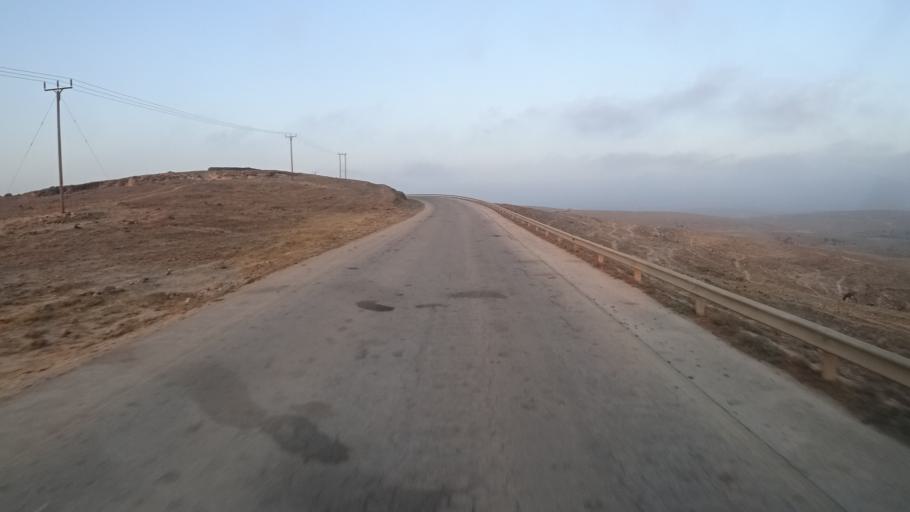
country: OM
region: Zufar
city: Salalah
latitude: 17.1336
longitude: 53.9270
